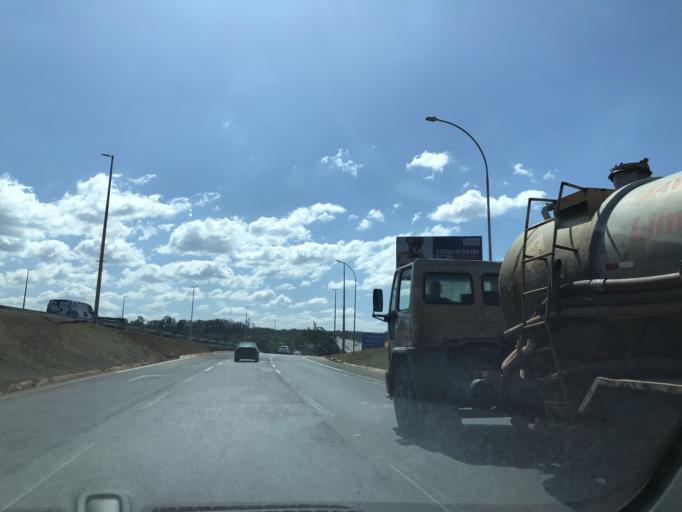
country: BR
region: Federal District
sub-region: Brasilia
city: Brasilia
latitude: -15.8572
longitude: -47.9330
